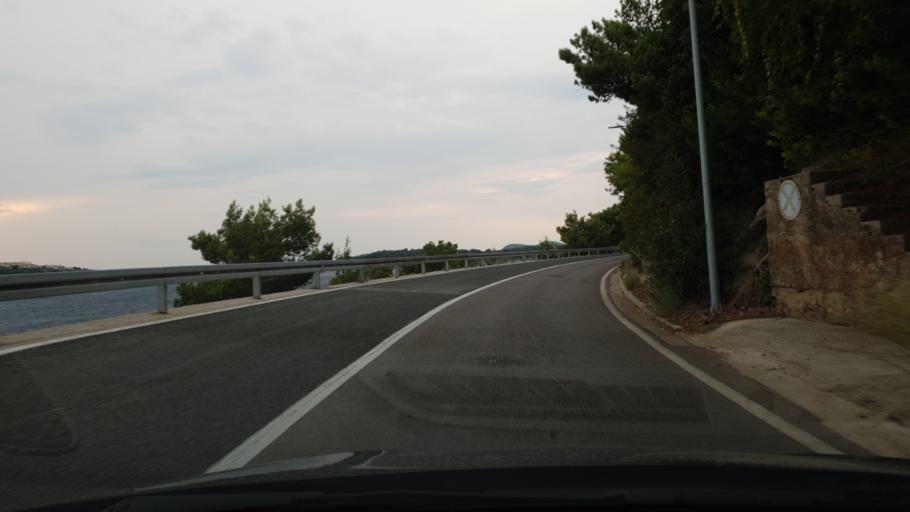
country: HR
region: Dubrovacko-Neretvanska
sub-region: Grad Dubrovnik
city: Mokosica
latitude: 42.6690
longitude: 18.0741
